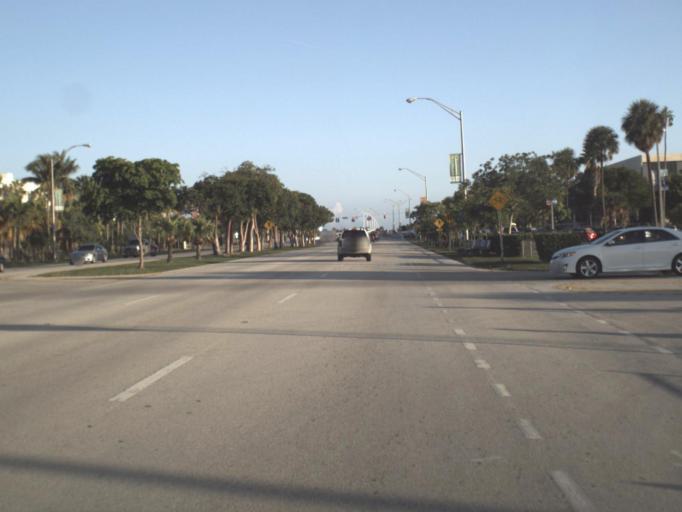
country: US
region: Florida
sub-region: Miami-Dade County
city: Key Biscayne
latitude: 25.7353
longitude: -80.1643
